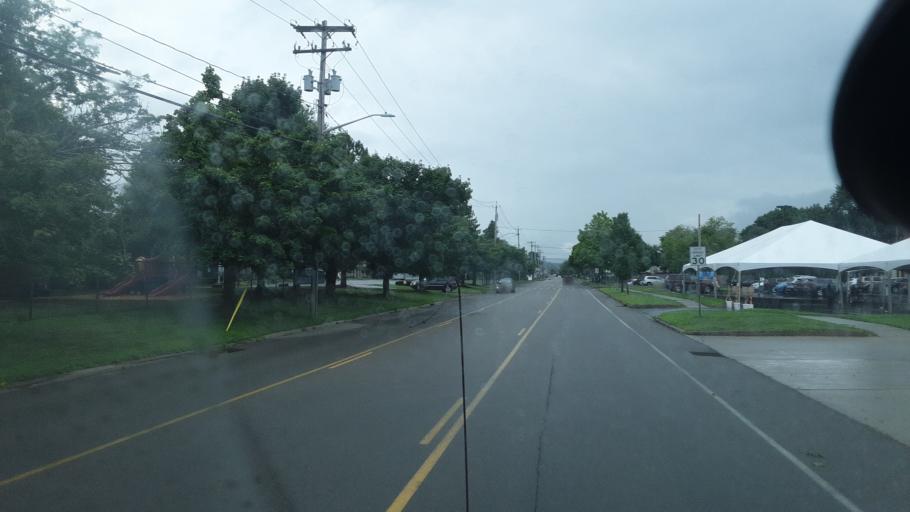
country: US
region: New York
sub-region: Cattaraugus County
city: Olean
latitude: 42.0851
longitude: -78.4437
